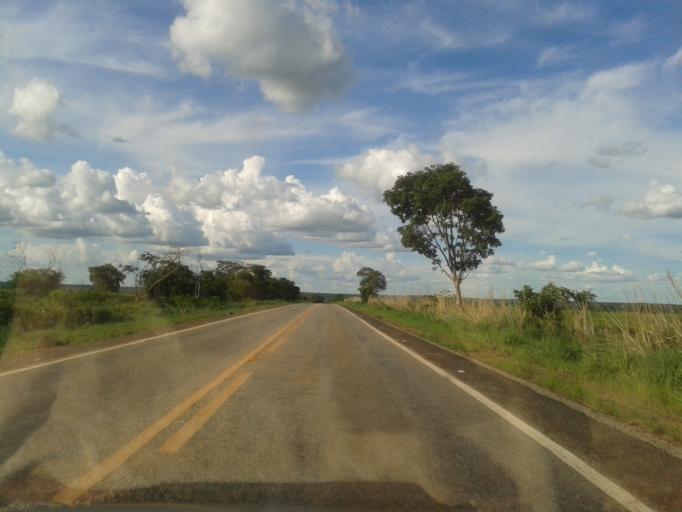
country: BR
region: Goias
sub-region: Mozarlandia
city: Mozarlandia
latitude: -14.5253
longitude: -50.4858
